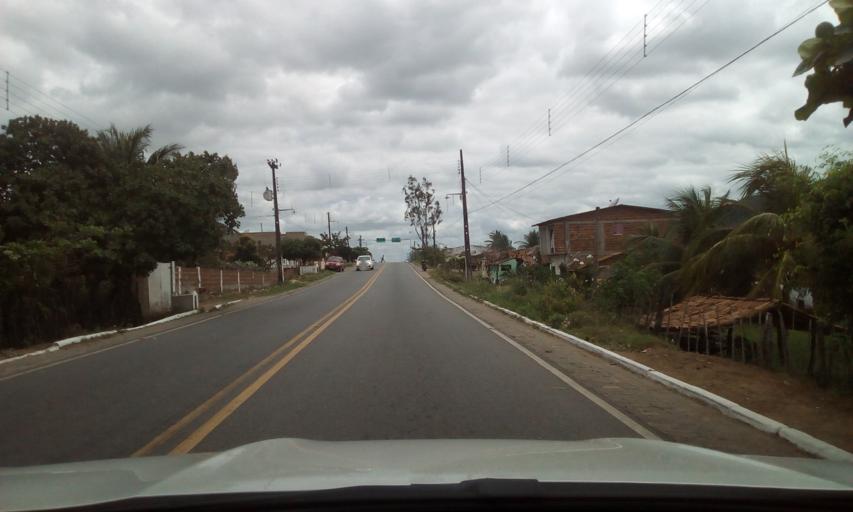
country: BR
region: Paraiba
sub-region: Serra Redonda
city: Alagoa Grande
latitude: -7.1823
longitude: -35.5892
